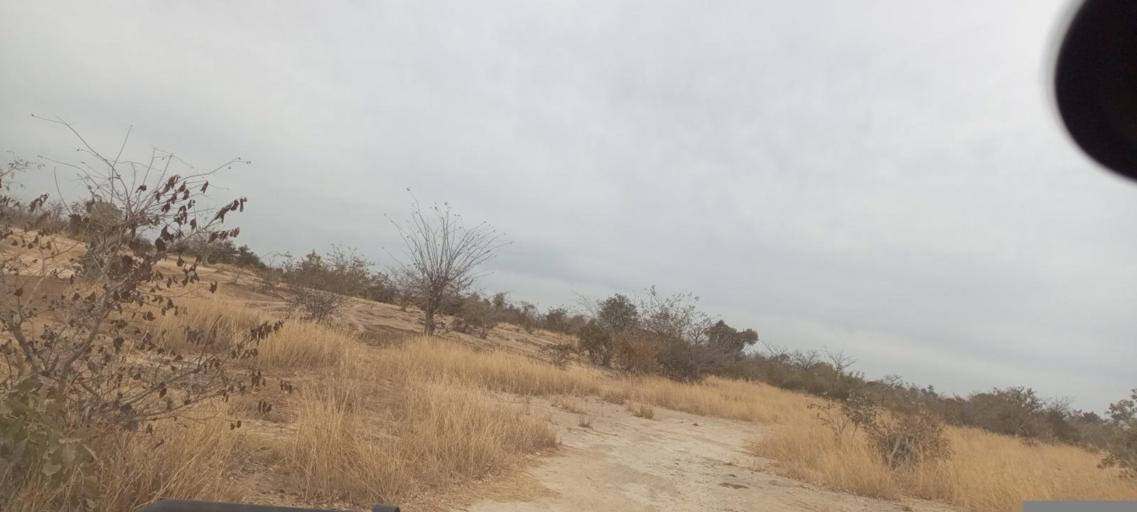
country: ML
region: Koulikoro
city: Kati
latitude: 12.7709
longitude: -8.3777
